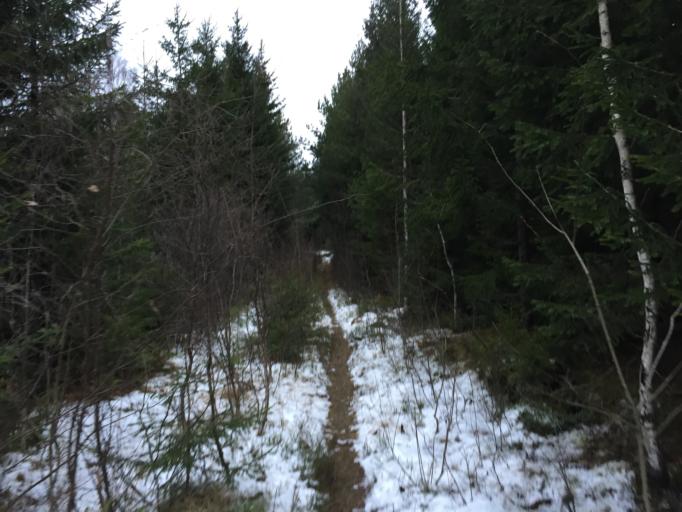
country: SE
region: Stockholm
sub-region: Salems Kommun
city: Ronninge
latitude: 59.2269
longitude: 17.6921
